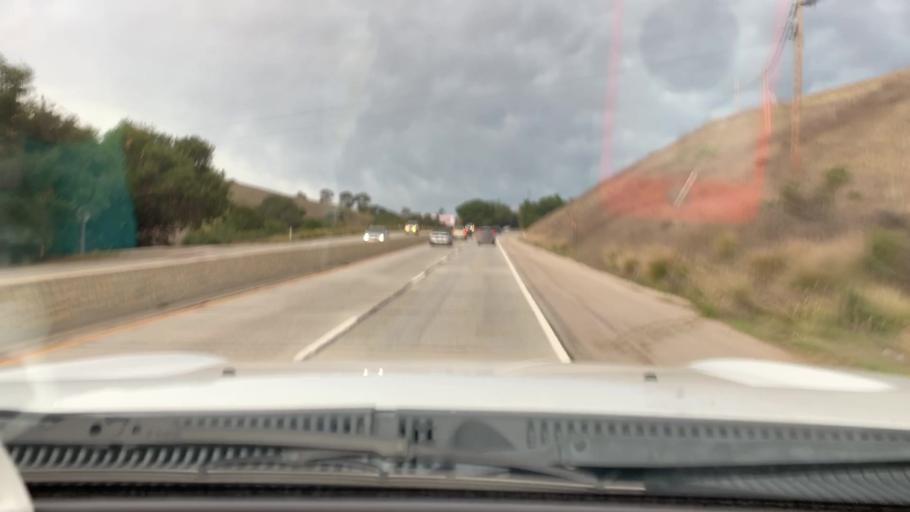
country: US
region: California
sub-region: San Luis Obispo County
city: San Luis Obispo
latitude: 35.3125
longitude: -120.6867
